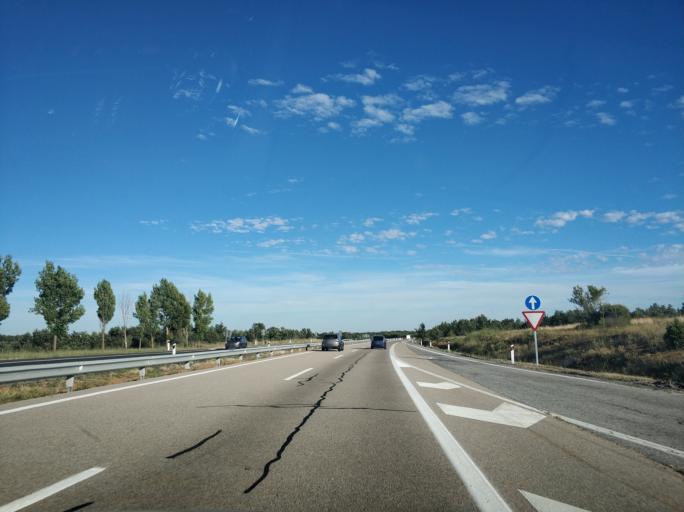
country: ES
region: Castille and Leon
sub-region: Provincia de Leon
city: Valverde de la Virgen
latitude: 42.6137
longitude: -5.7322
